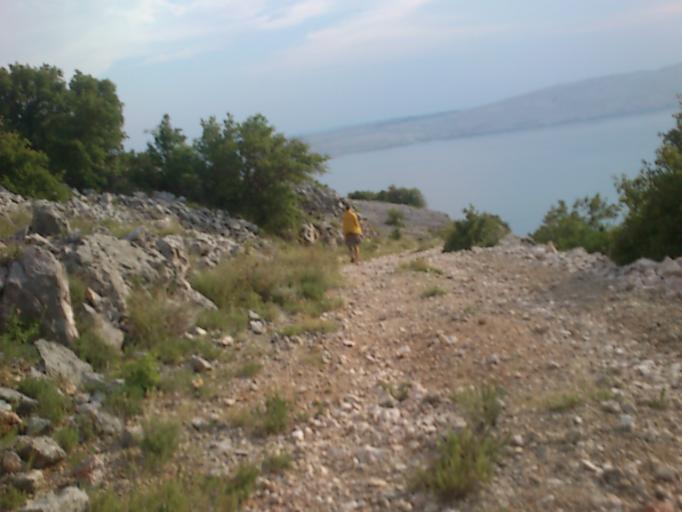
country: HR
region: Primorsko-Goranska
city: Banjol
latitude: 44.7633
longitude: 14.8948
